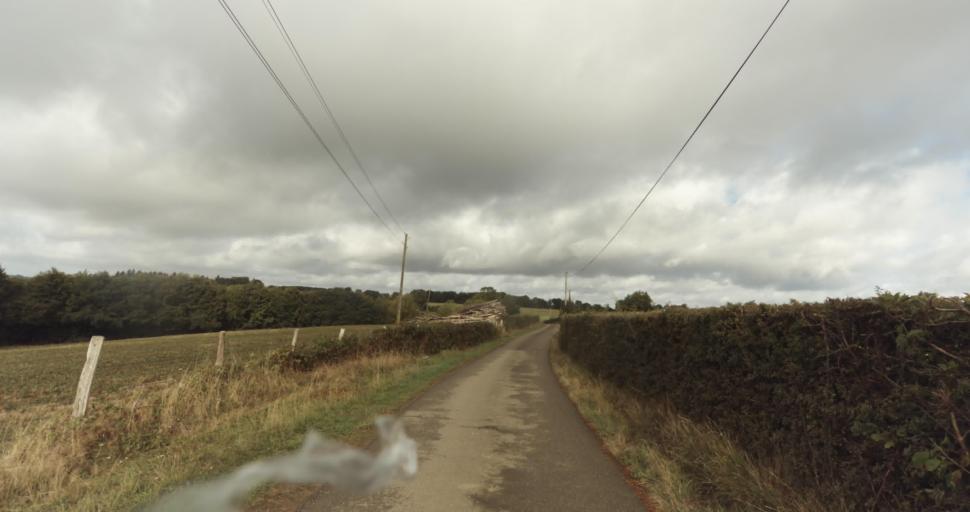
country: FR
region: Lower Normandy
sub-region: Departement de l'Orne
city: Gace
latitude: 48.8488
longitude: 0.3150
